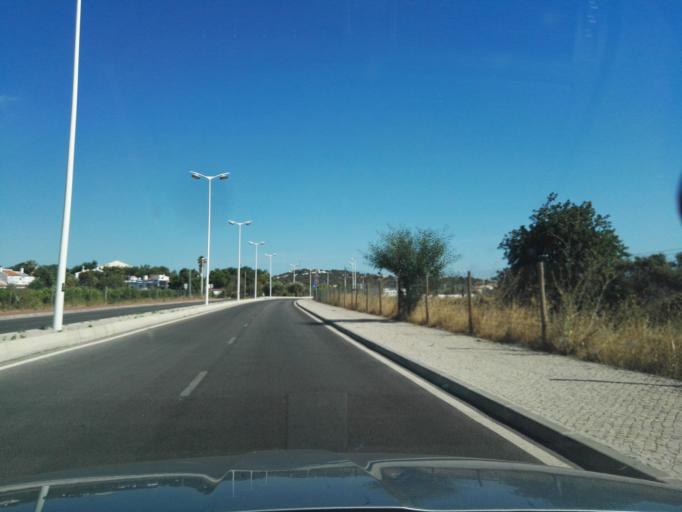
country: PT
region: Faro
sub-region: Sao Bras de Alportel
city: Sao Bras de Alportel
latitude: 37.1583
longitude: -7.8821
